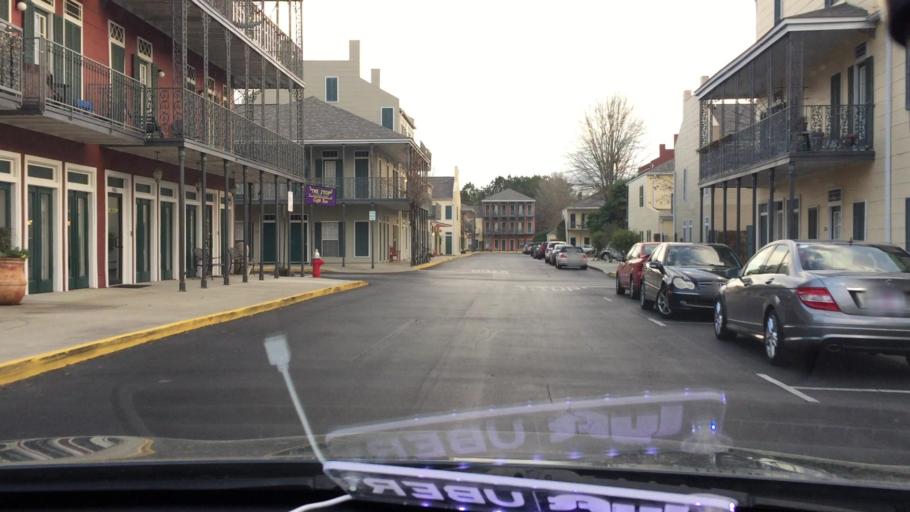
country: US
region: Alabama
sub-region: Lee County
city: Auburn
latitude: 32.5780
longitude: -85.4897
